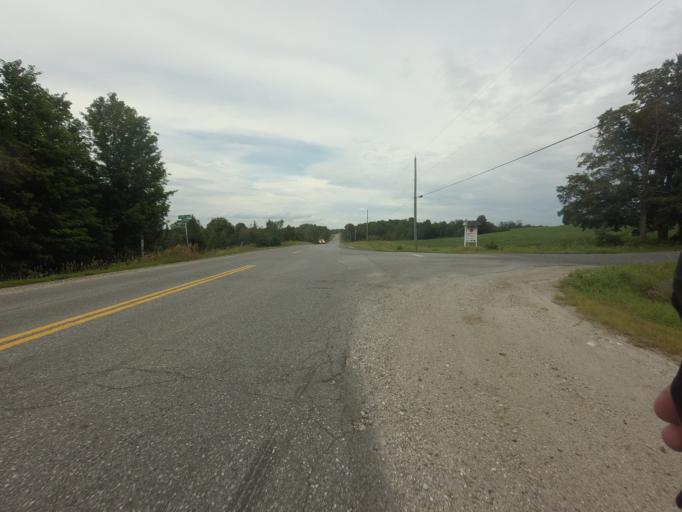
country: CA
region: Ontario
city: Carleton Place
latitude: 45.1251
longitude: -76.3399
